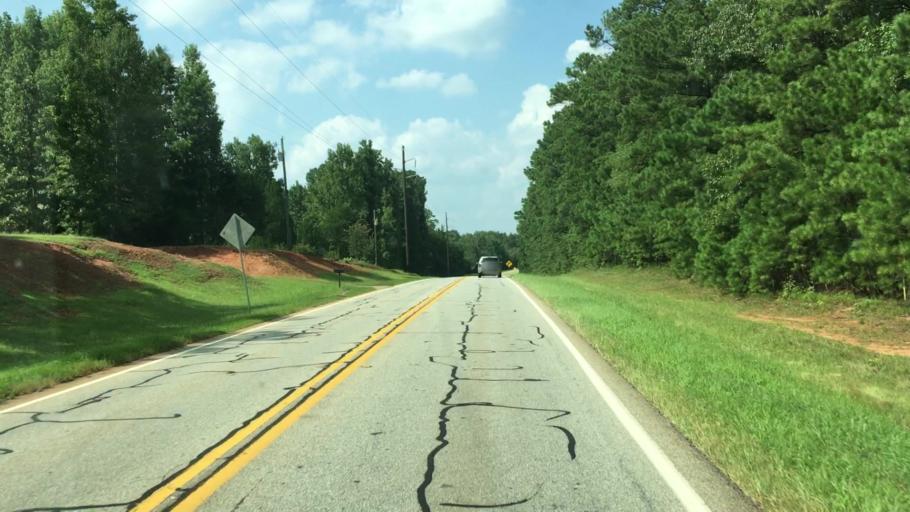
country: US
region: Georgia
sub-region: Jasper County
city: Monticello
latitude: 33.2795
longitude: -83.7133
